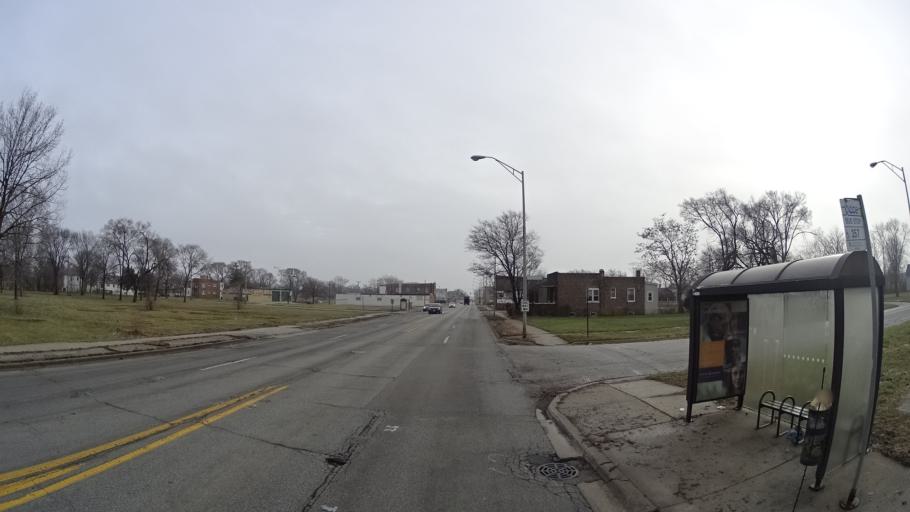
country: US
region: Illinois
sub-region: Cook County
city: Chicago Heights
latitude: 41.5060
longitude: -87.6310
